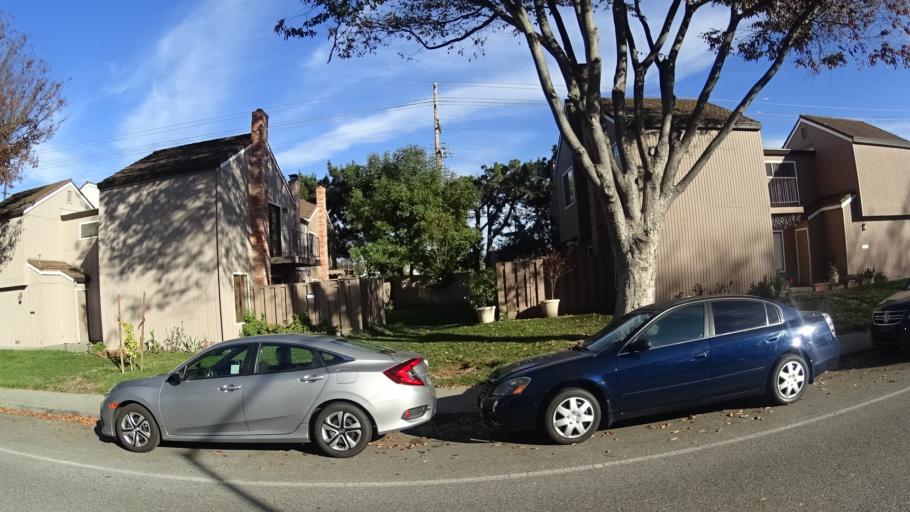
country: US
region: California
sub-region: Santa Clara County
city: Santa Clara
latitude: 37.3659
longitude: -121.9693
